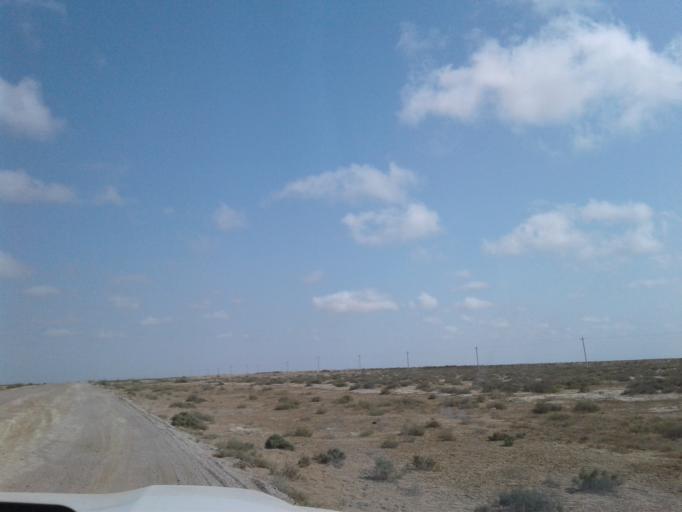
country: IR
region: Golestan
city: Gomishan
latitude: 37.6562
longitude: 53.9327
